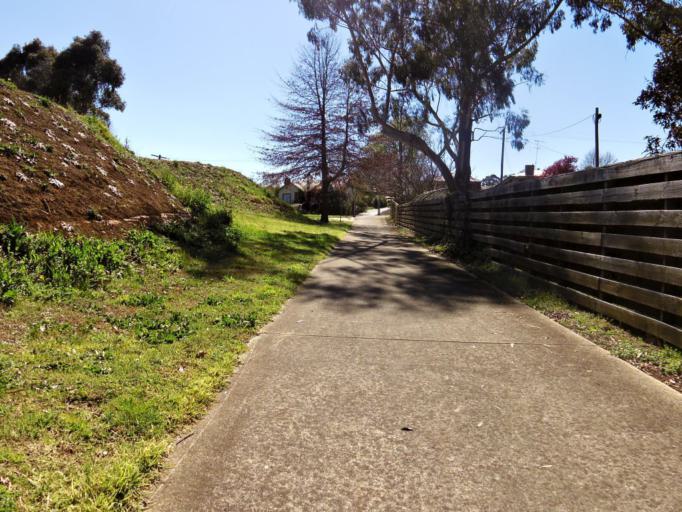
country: AU
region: Victoria
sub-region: Baw Baw
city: Warragul
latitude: -38.1562
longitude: 145.9210
